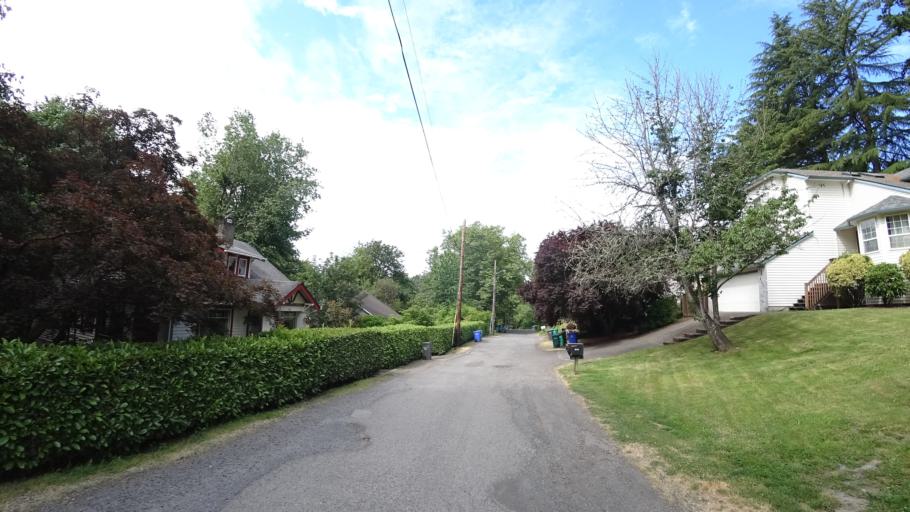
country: US
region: Oregon
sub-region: Clackamas County
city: Lake Oswego
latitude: 45.4561
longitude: -122.6872
